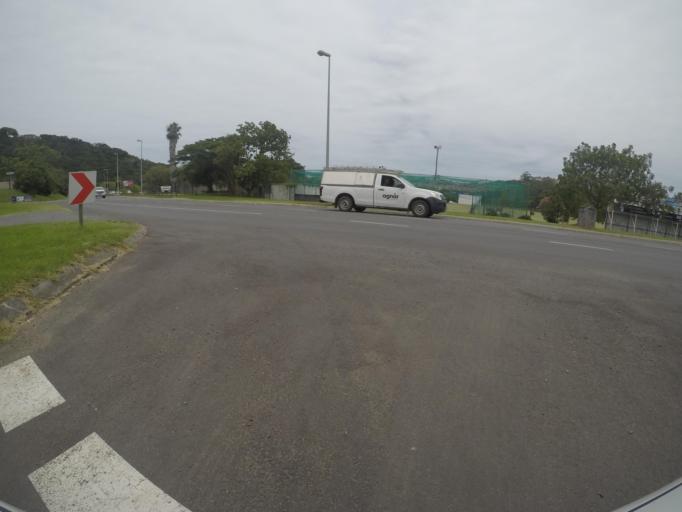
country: ZA
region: Eastern Cape
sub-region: Buffalo City Metropolitan Municipality
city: East London
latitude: -32.9733
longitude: 27.9318
